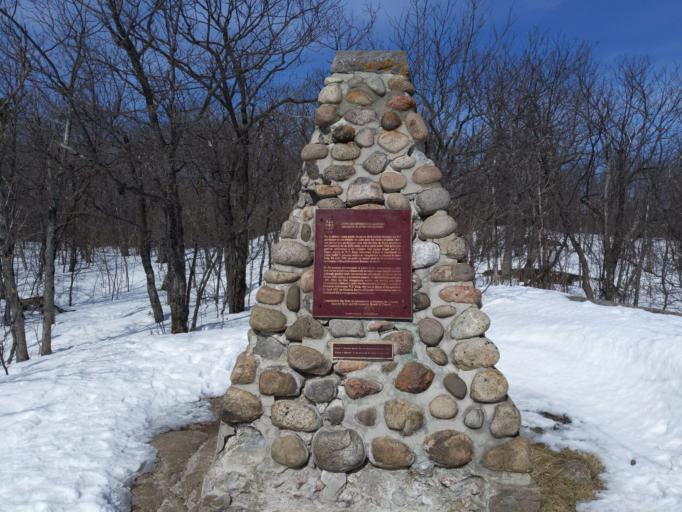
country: CA
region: Quebec
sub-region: Outaouais
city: Gatineau
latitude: 45.4891
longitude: -75.8626
